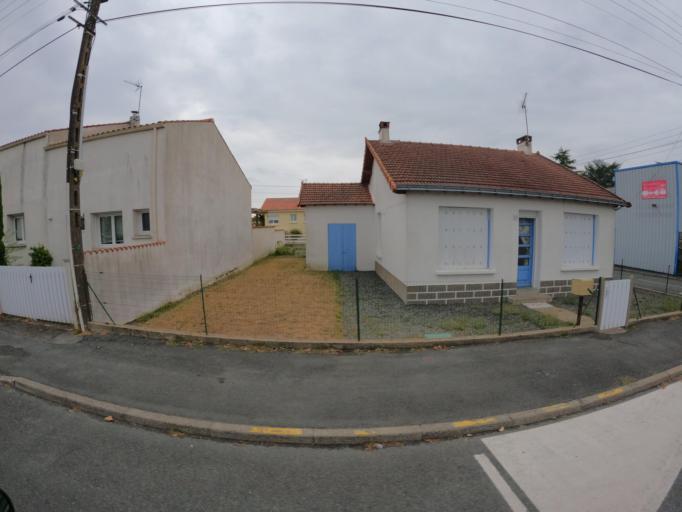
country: FR
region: Pays de la Loire
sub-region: Departement de la Vendee
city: Montaigu
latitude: 46.9796
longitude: -1.3076
